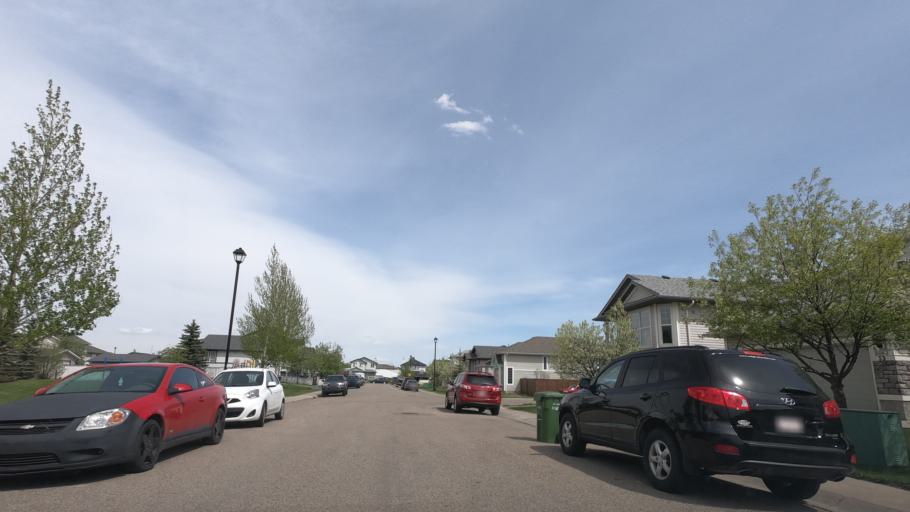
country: CA
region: Alberta
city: Airdrie
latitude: 51.3062
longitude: -114.0231
